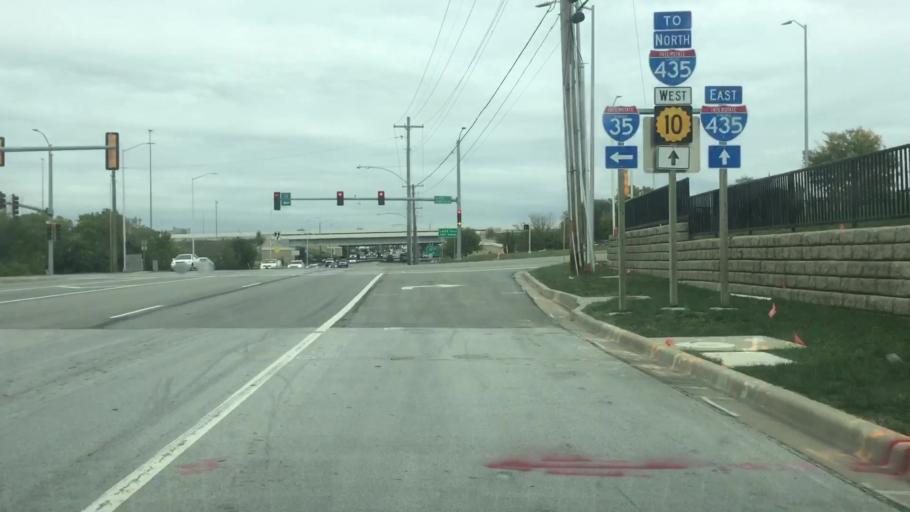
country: US
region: Kansas
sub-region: Johnson County
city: Lenexa
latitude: 38.9394
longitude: -94.7606
